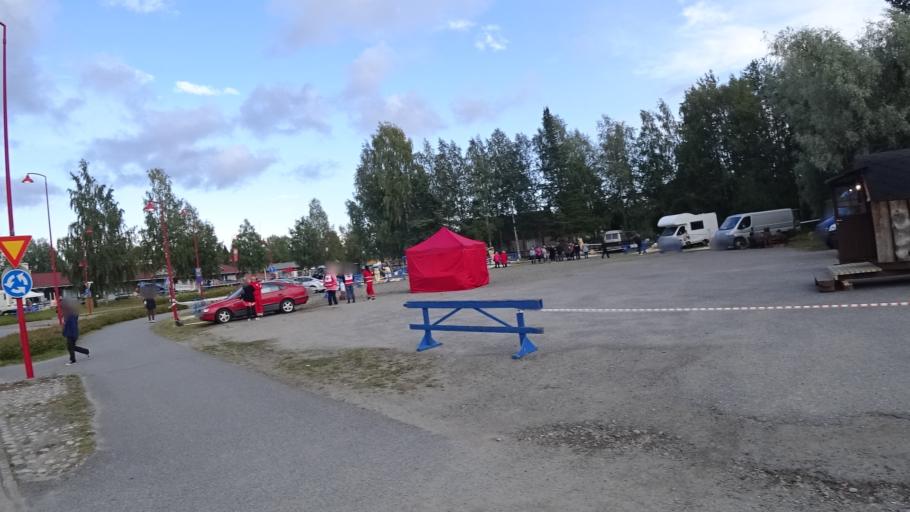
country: FI
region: North Karelia
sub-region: Joensuu
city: Ilomantsi
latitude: 62.6714
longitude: 30.9321
